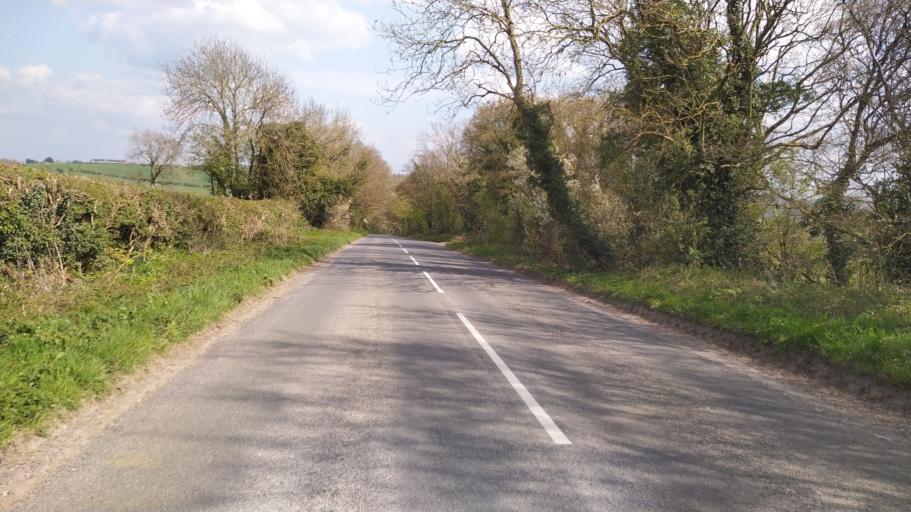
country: GB
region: England
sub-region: Somerset
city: Frome
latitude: 51.2340
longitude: -2.3599
